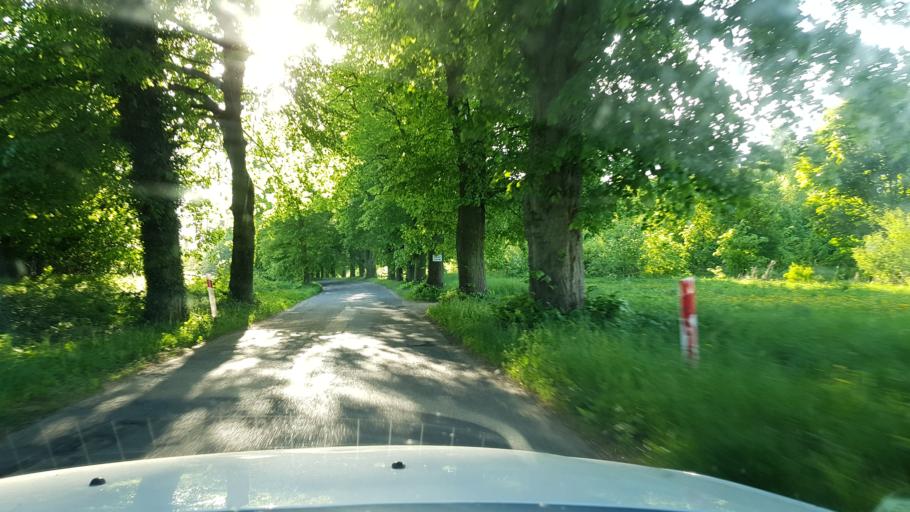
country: PL
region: West Pomeranian Voivodeship
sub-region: Powiat lobeski
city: Dobra
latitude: 53.5872
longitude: 15.3017
